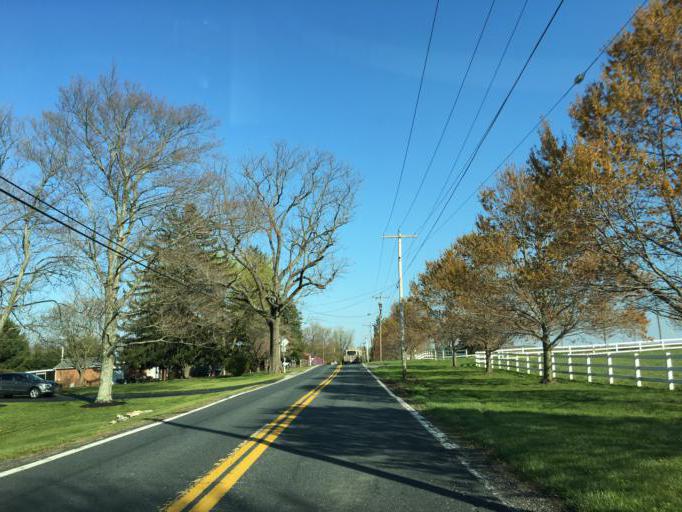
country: US
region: Maryland
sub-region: Baltimore County
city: Perry Hall
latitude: 39.4400
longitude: -76.4946
